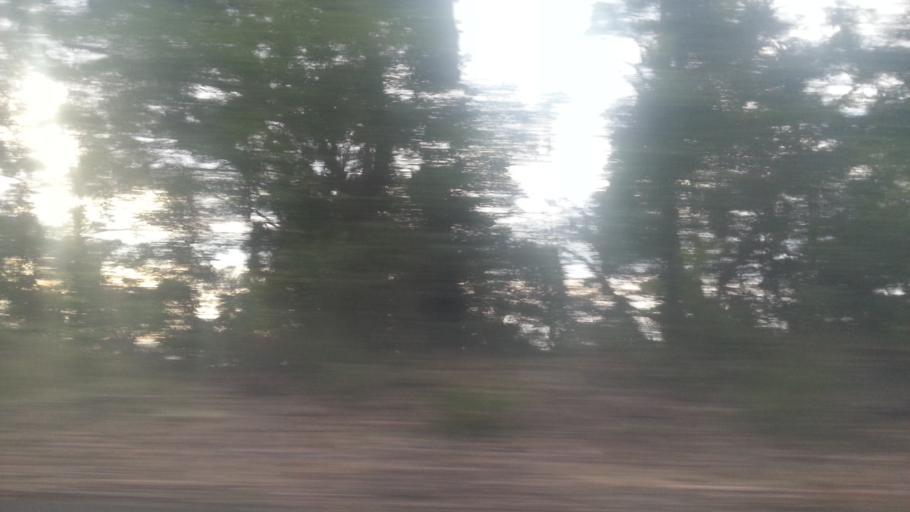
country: AU
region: New South Wales
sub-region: Wollongong
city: Mount Ousley
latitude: -34.3857
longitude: 150.8548
